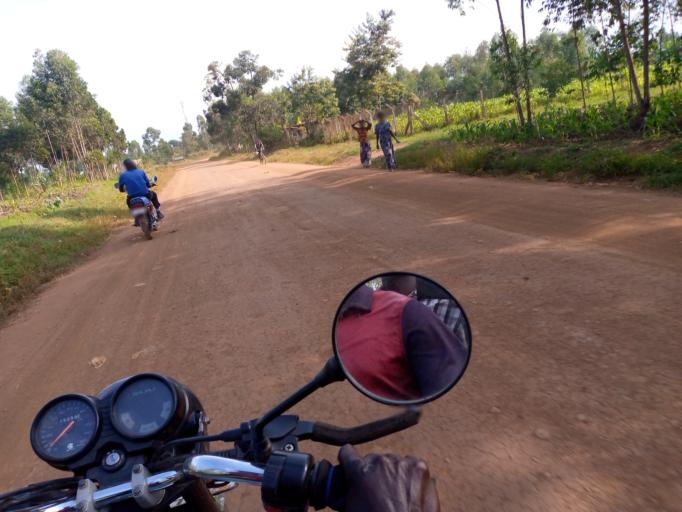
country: UG
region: Eastern Region
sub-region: Mbale District
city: Mbale
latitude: 1.0661
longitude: 34.1556
